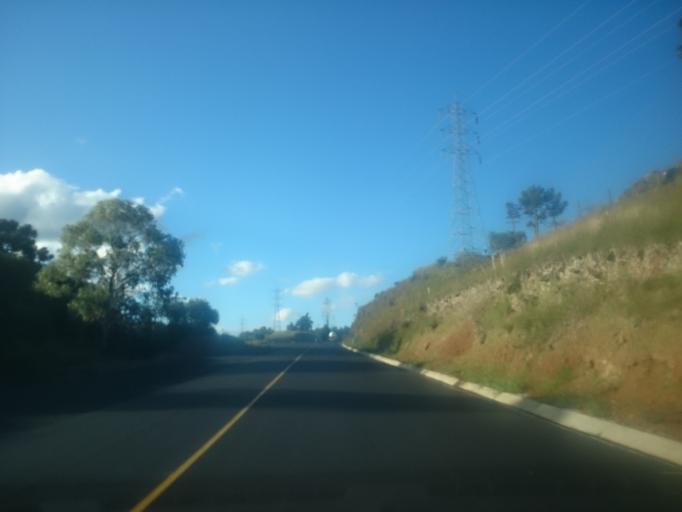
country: BR
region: Santa Catarina
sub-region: Sao Joaquim
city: Sao Joaquim
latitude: -28.0579
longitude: -50.0738
